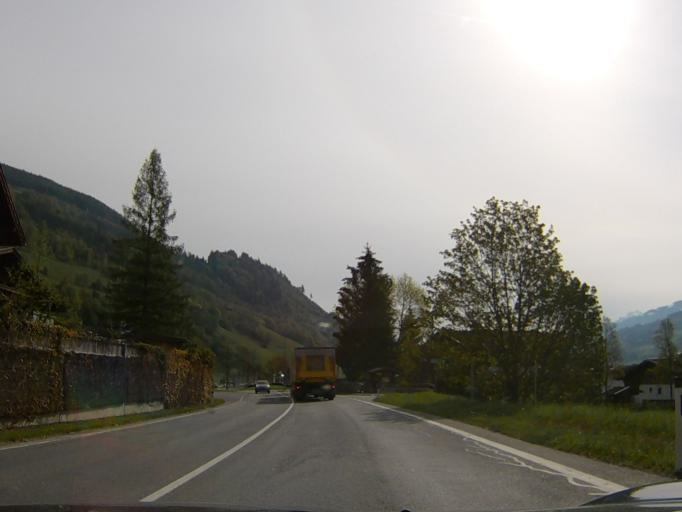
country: AT
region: Salzburg
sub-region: Politischer Bezirk Zell am See
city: Niedernsill
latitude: 47.2839
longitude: 12.6368
